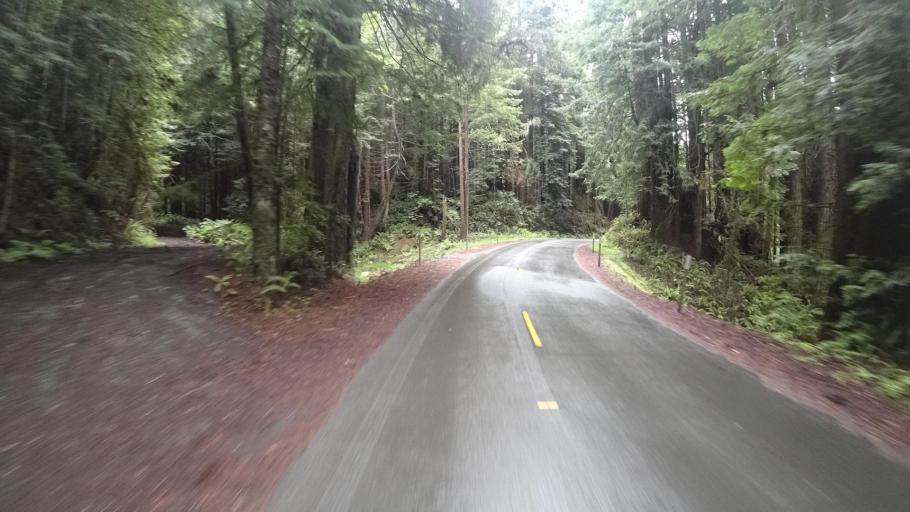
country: US
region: California
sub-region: Humboldt County
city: Bayside
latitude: 40.8208
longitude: -124.0307
